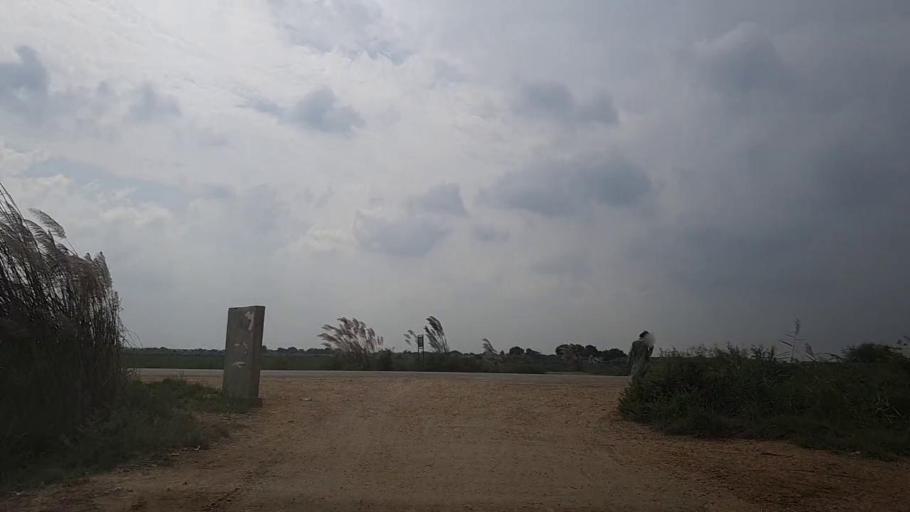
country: PK
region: Sindh
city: Mirpur Batoro
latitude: 24.5834
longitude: 68.1196
